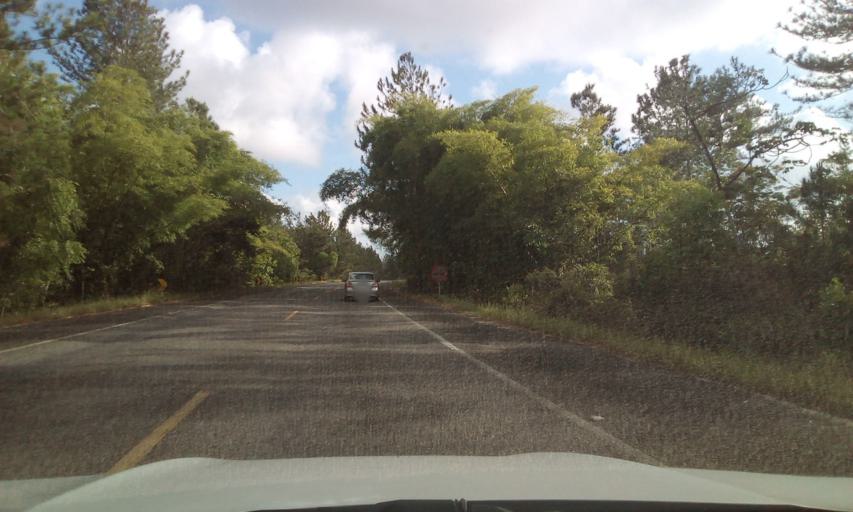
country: BR
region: Bahia
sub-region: Entre Rios
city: Entre Rios
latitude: -12.1533
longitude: -37.8019
